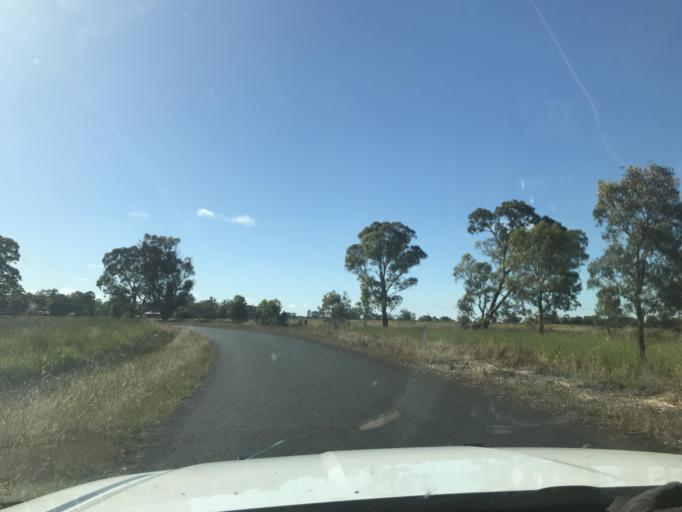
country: AU
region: Victoria
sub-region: Horsham
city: Horsham
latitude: -37.0299
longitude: 141.7193
